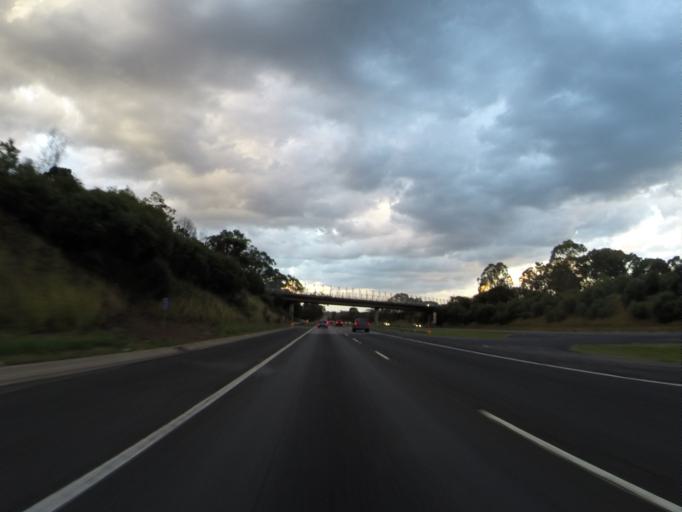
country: AU
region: New South Wales
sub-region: Campbelltown Municipality
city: Glen Alpine
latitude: -34.1073
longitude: 150.7616
